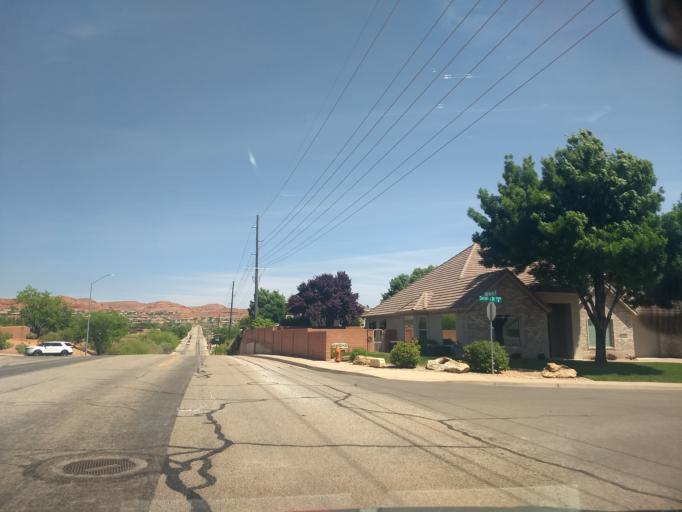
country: US
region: Utah
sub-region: Washington County
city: Santa Clara
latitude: 37.1429
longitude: -113.6374
